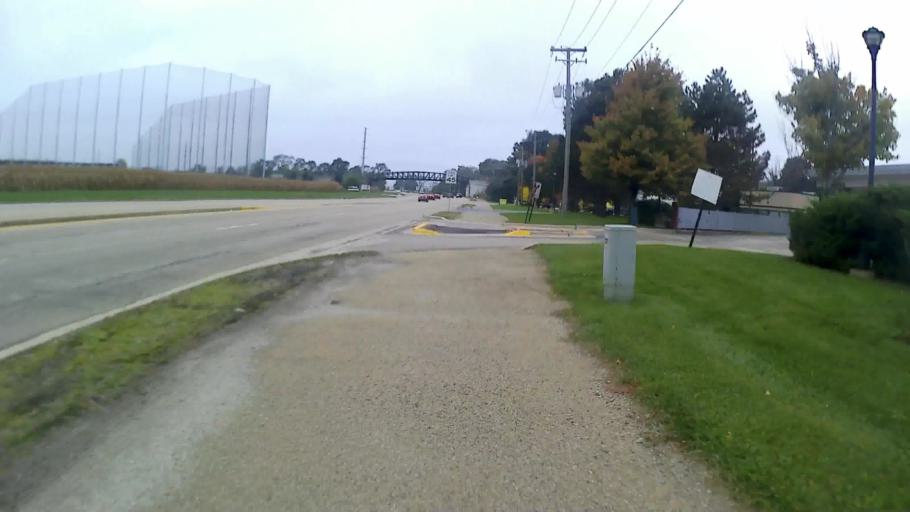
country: US
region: Illinois
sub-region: DuPage County
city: Warrenville
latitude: 41.8101
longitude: -88.2042
